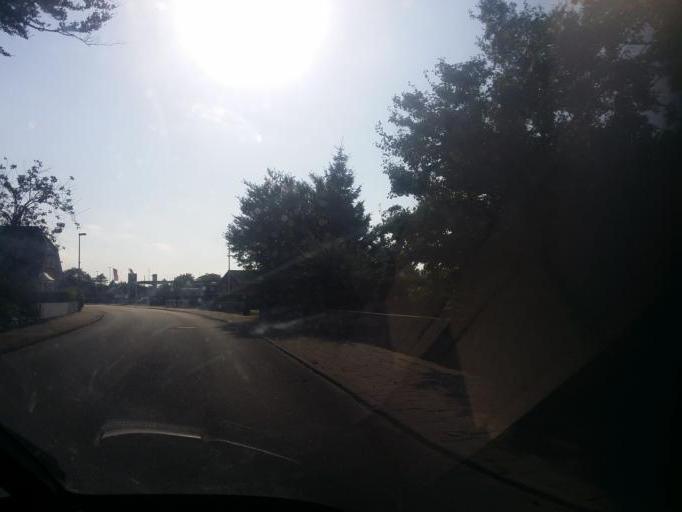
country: DE
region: Schleswig-Holstein
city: Rodenas
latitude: 54.9628
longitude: 8.7010
